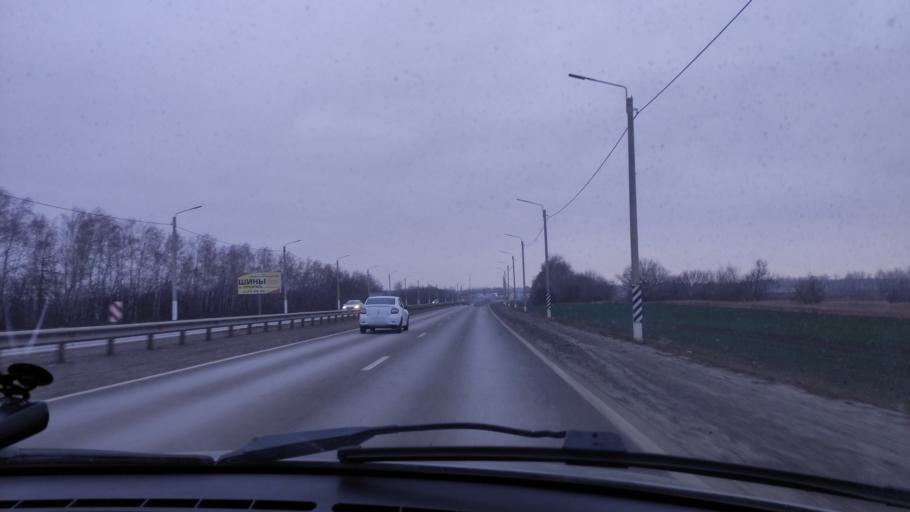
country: RU
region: Tambov
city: Komsomolets
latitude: 52.7262
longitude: 41.3433
